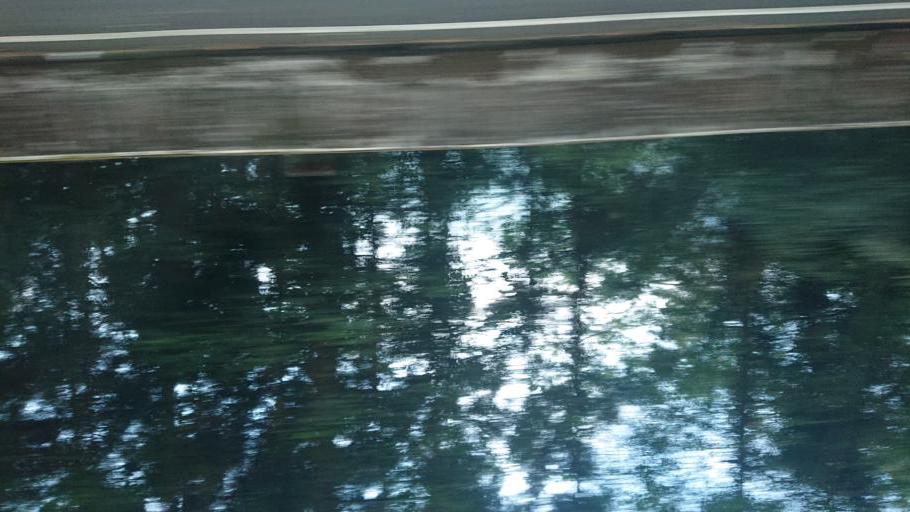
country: TW
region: Taiwan
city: Lugu
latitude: 23.4823
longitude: 120.7467
